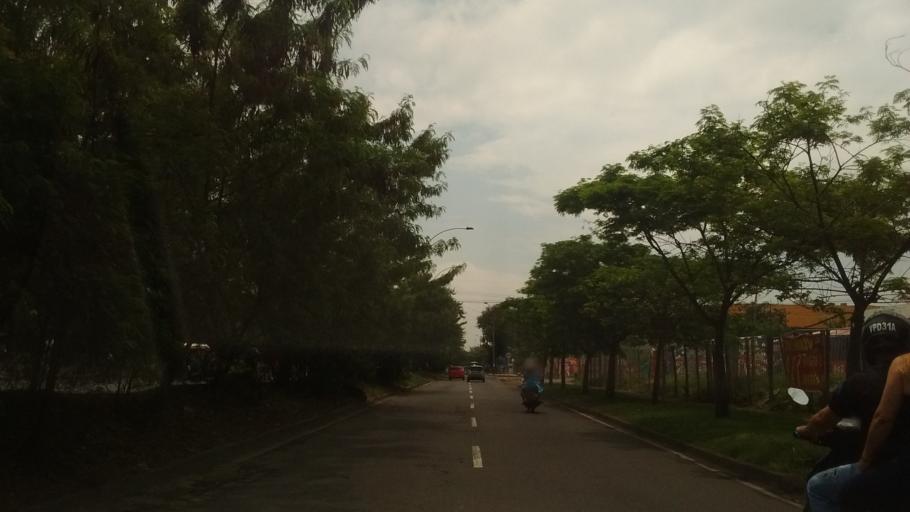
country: CO
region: Valle del Cauca
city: Cali
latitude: 3.4712
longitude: -76.4866
